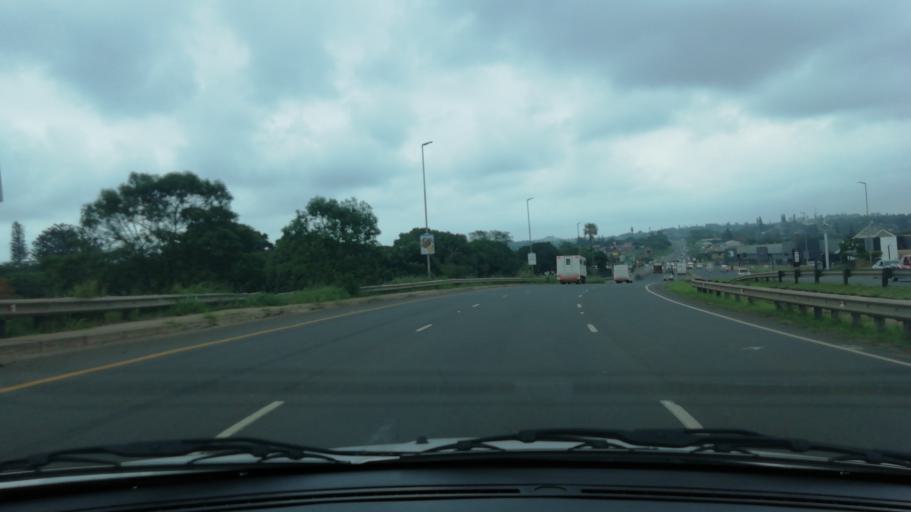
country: ZA
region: KwaZulu-Natal
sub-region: uThungulu District Municipality
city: Empangeni
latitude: -28.7668
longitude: 31.9110
